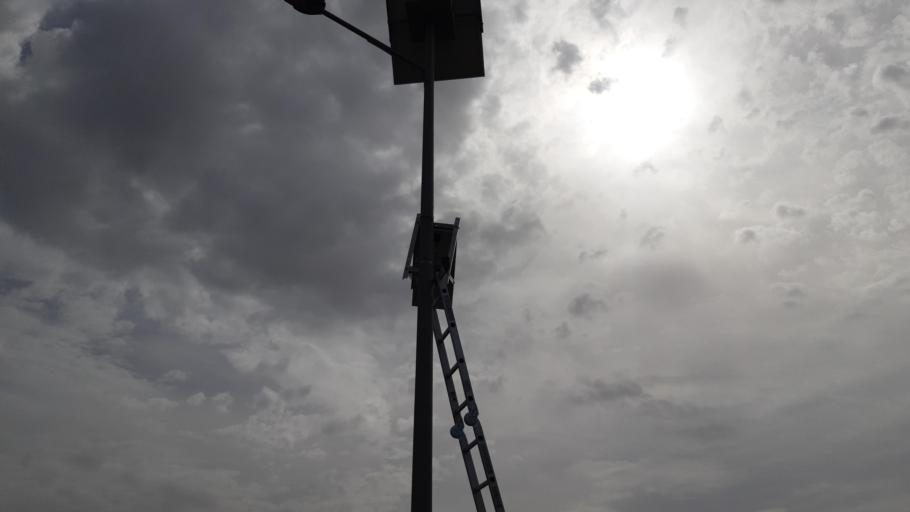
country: TN
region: Al Munastir
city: Al Baqalitah
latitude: 35.5611
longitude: 11.0093
